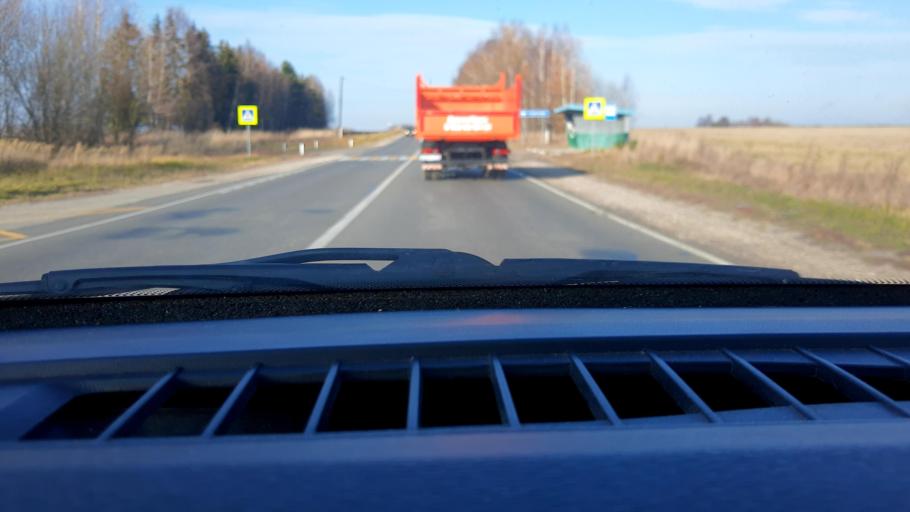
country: RU
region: Nizjnij Novgorod
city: Gorodets
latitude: 56.6246
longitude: 43.5483
